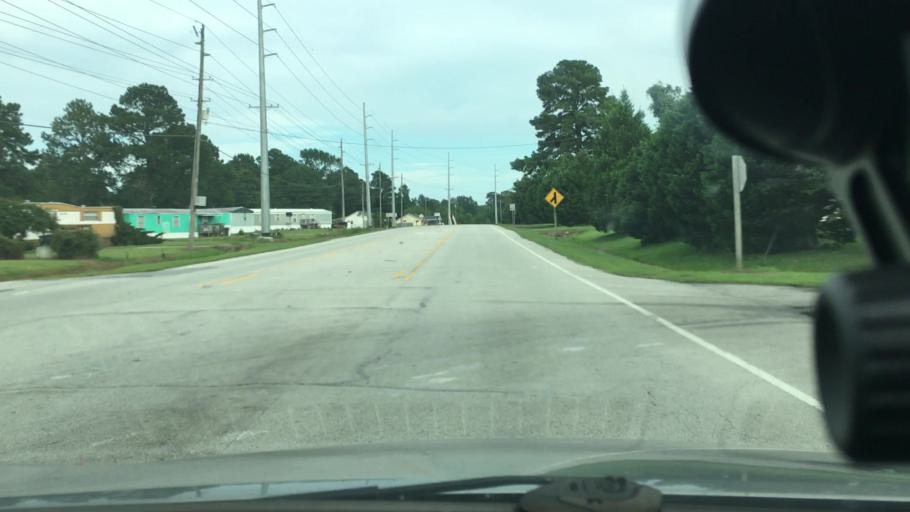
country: US
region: North Carolina
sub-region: Pitt County
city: Windsor
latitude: 35.5563
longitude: -77.3327
